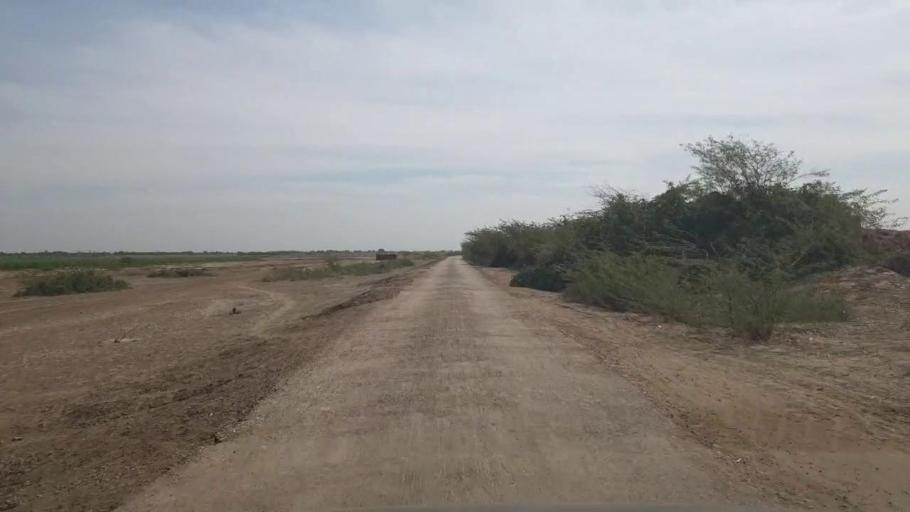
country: PK
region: Sindh
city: Kunri
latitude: 25.2703
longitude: 69.6005
